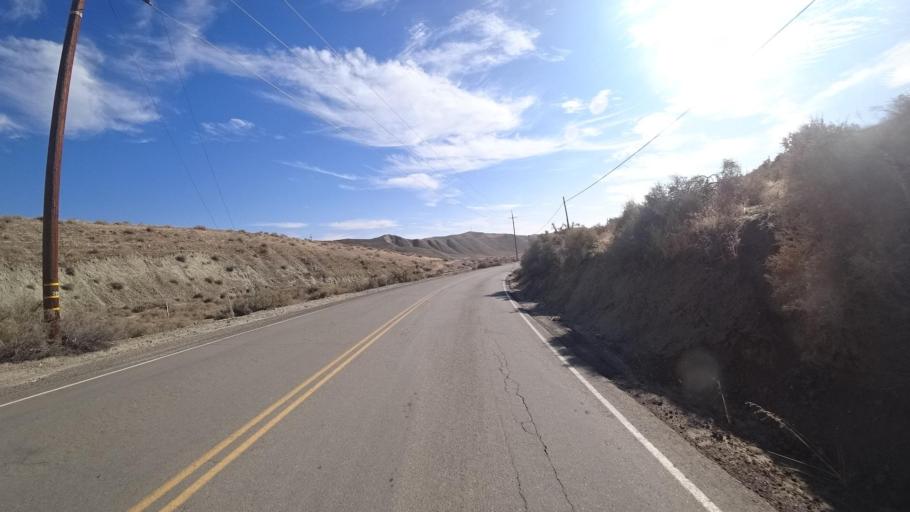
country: US
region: California
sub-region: Kern County
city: Oildale
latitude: 35.5680
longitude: -118.9574
